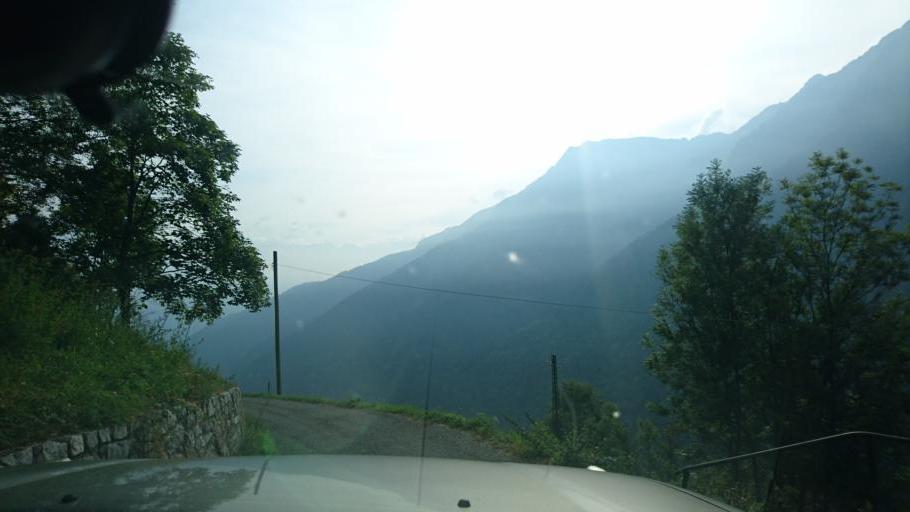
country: IT
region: Lombardy
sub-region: Provincia di Brescia
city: Paisco Loveno
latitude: 46.0689
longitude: 10.2591
